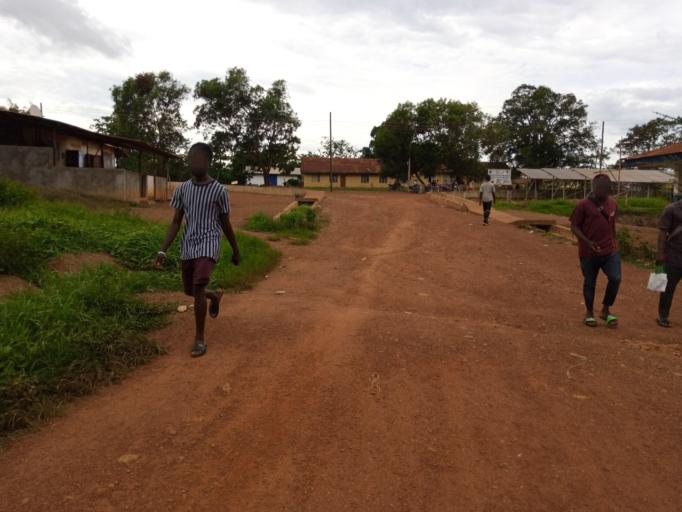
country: SL
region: Southern Province
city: Largo
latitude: 8.1123
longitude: -12.0713
